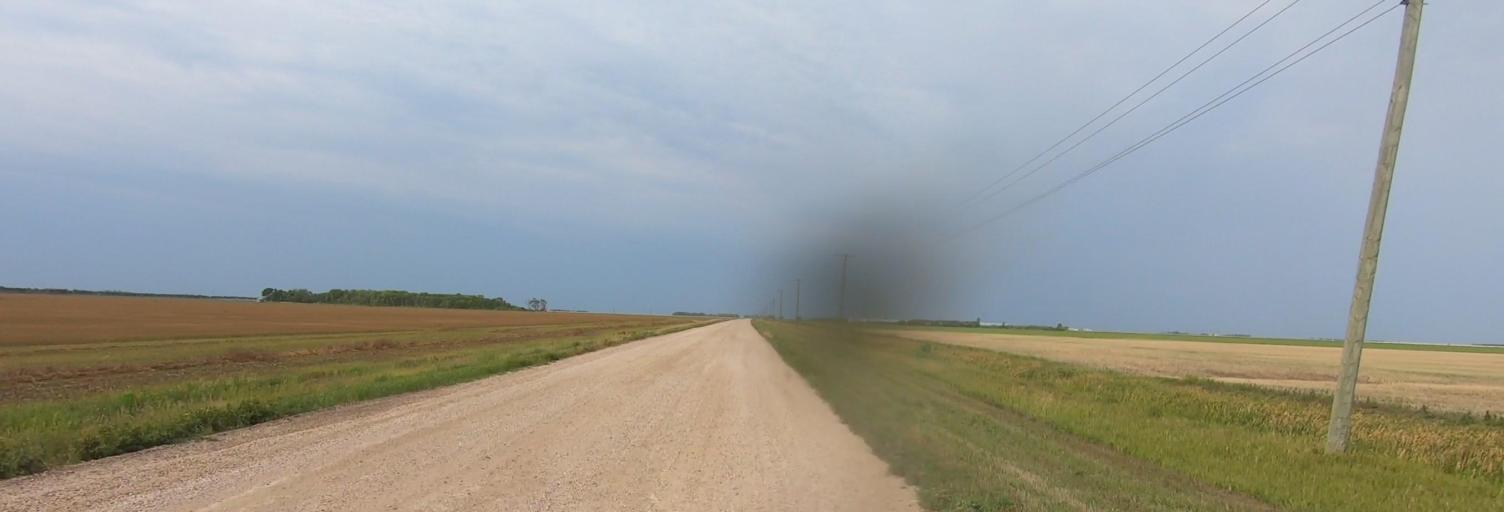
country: CA
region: Manitoba
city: Morris
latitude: 49.5764
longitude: -97.3077
